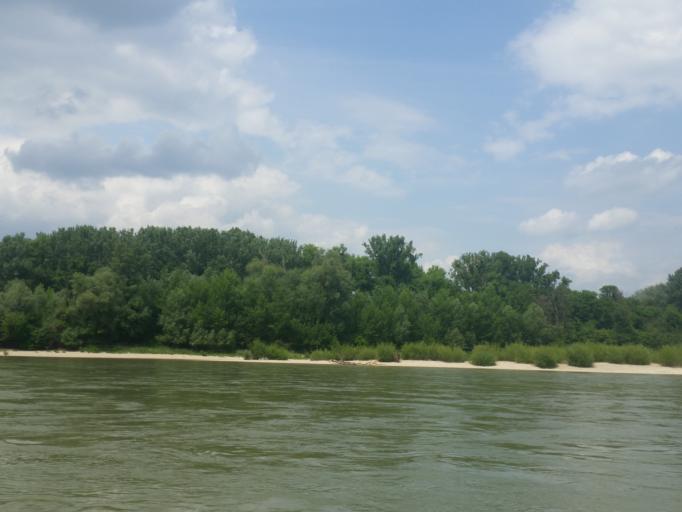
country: AT
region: Lower Austria
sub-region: Politischer Bezirk Bruck an der Leitha
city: Hainburg an der Donau
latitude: 48.1490
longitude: 16.9343
